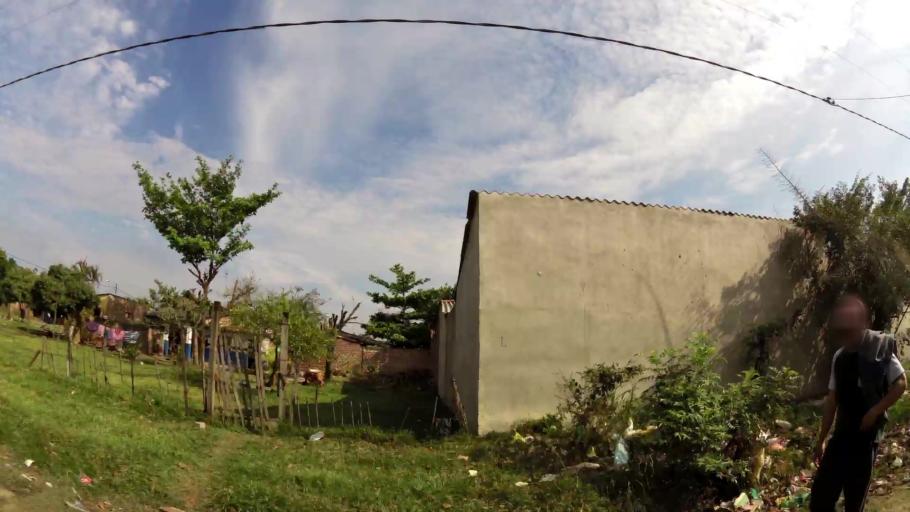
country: BO
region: Santa Cruz
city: Santa Cruz de la Sierra
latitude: -17.7359
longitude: -63.1341
